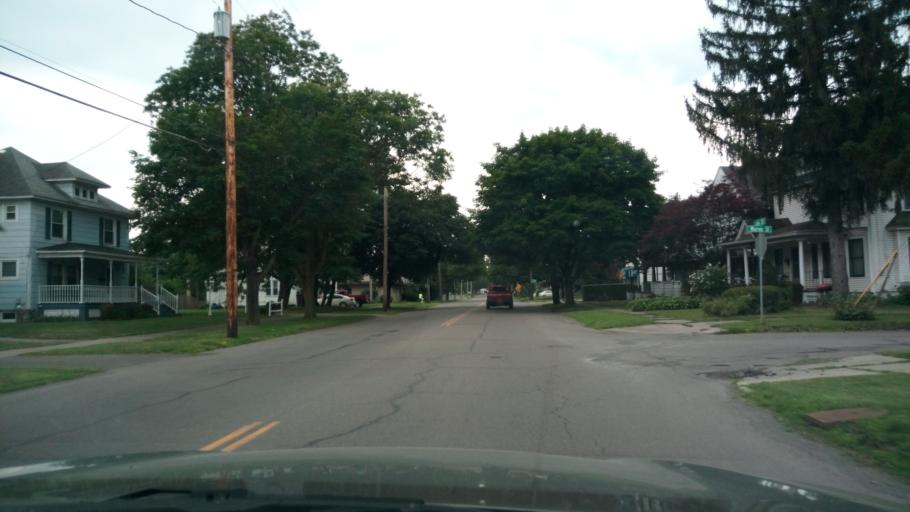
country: US
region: New York
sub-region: Chemung County
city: Elmira Heights
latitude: 42.1142
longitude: -76.8080
